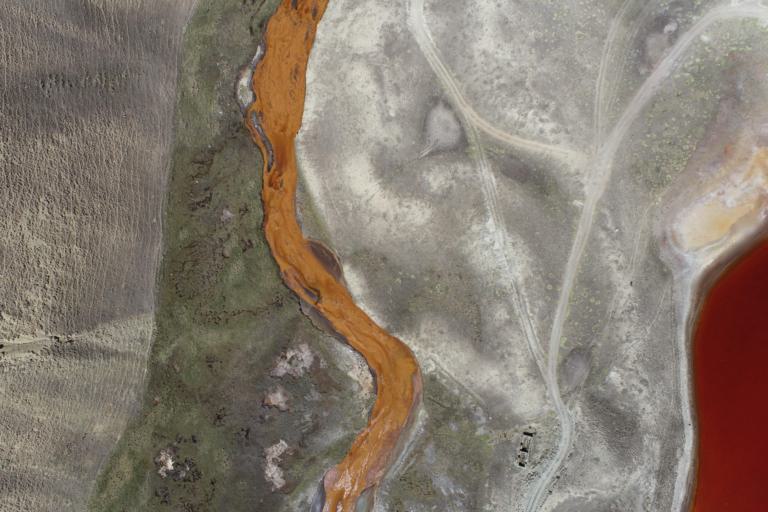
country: BO
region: La Paz
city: La Paz
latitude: -16.3424
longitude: -68.1587
